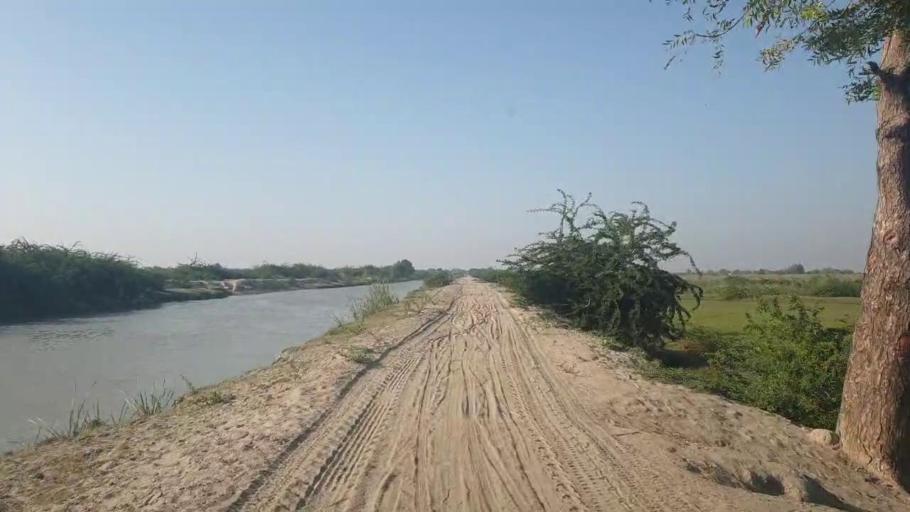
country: PK
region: Sindh
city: Tando Bago
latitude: 24.7259
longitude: 68.9237
